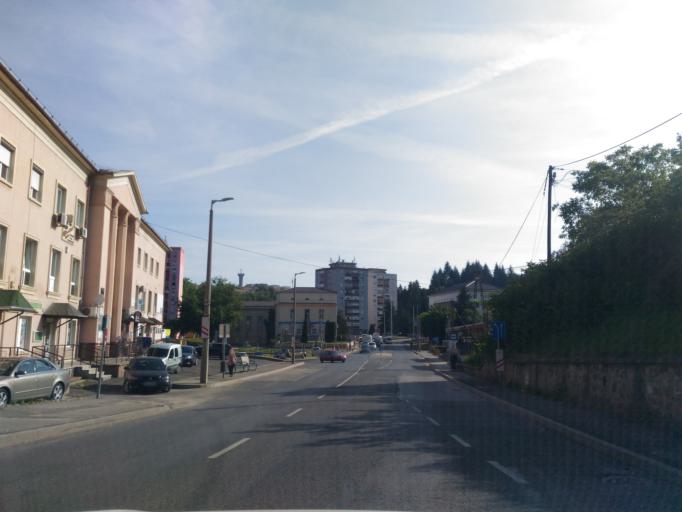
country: HU
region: Baranya
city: Komlo
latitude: 46.1896
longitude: 18.2595
